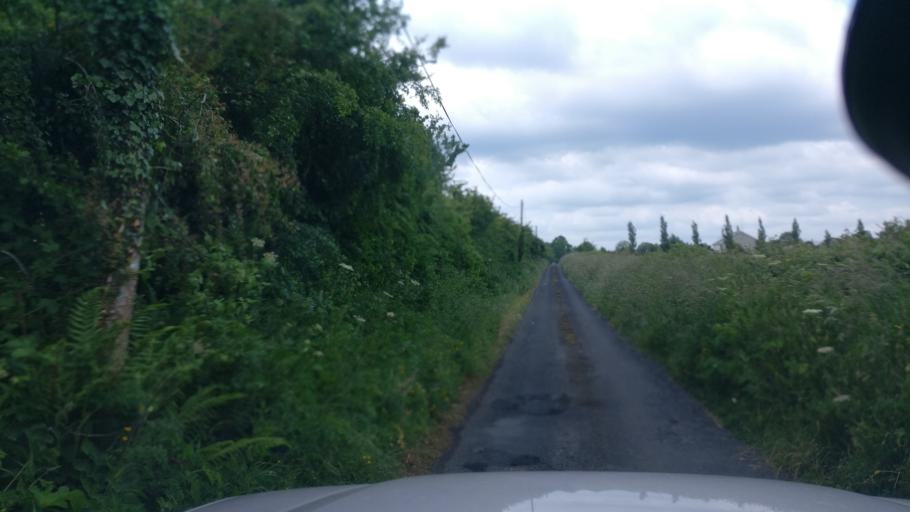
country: IE
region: Connaught
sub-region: County Galway
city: Ballinasloe
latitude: 53.2732
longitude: -8.3727
